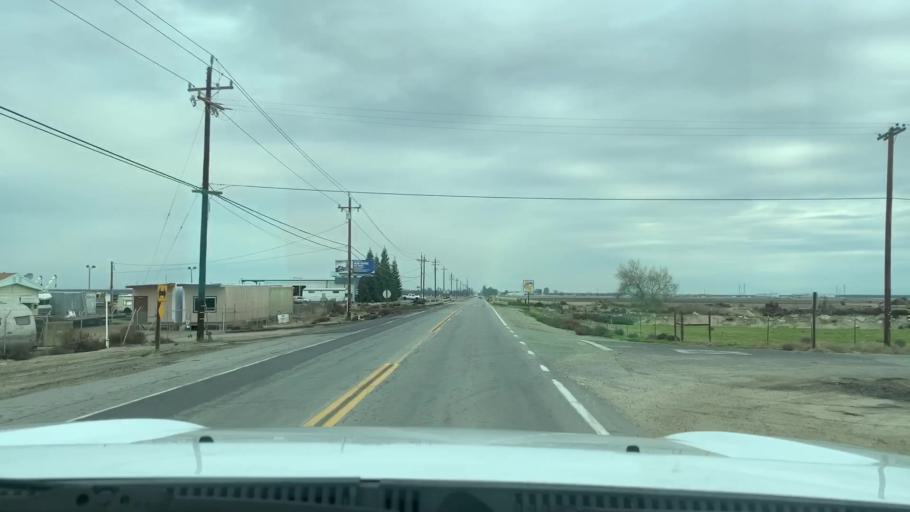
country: US
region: California
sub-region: Kern County
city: Rosedale
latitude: 35.3681
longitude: -119.2521
